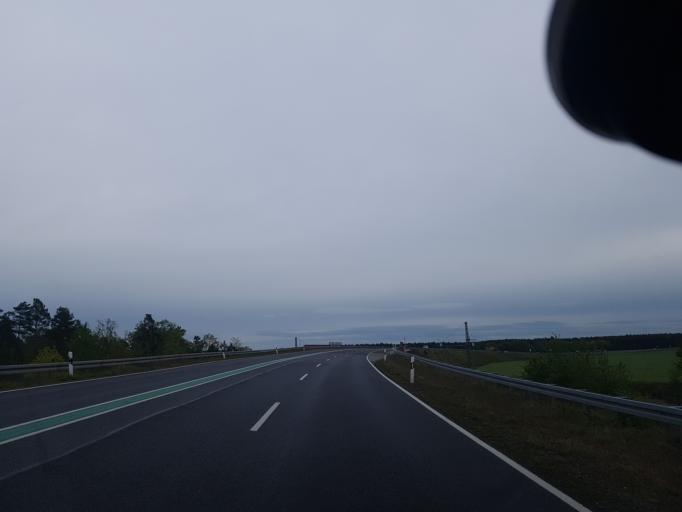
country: DE
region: Brandenburg
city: Drebkau
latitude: 51.6382
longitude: 14.1998
